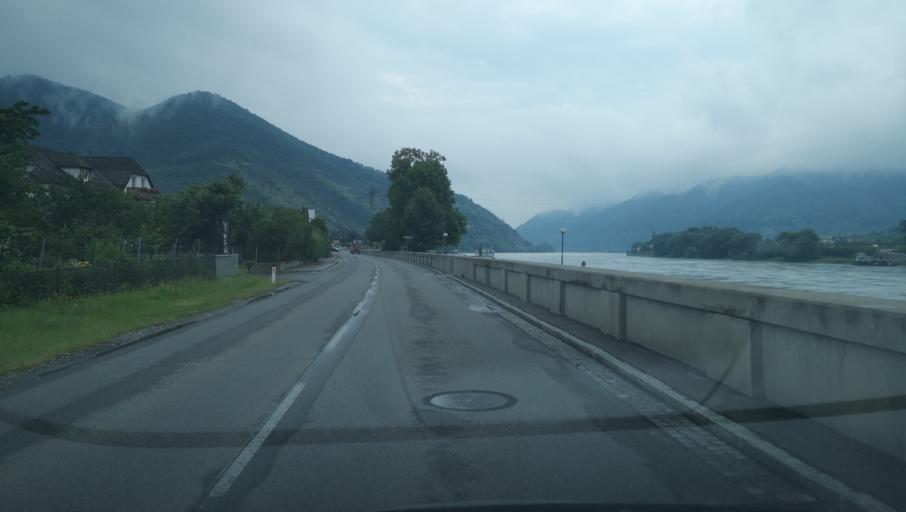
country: AT
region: Lower Austria
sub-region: Politischer Bezirk Krems
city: Spitz
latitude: 48.3601
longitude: 15.4141
